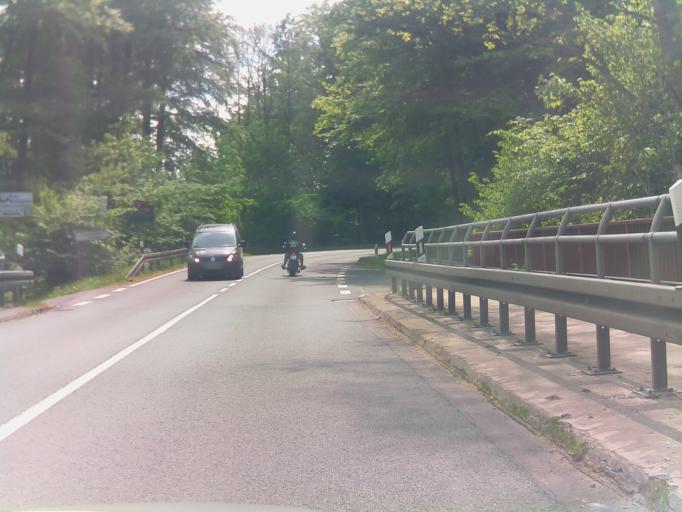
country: DE
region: Saxony-Anhalt
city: Huttenrode
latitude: 51.7409
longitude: 10.9220
